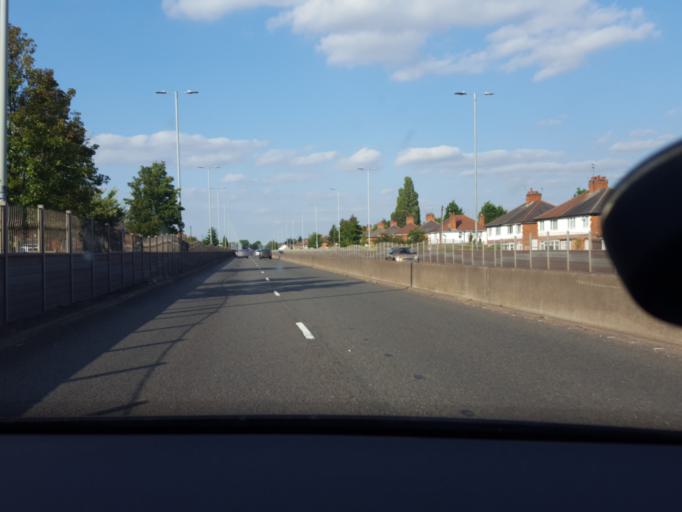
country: GB
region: England
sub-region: Leicestershire
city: Blaby
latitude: 52.6064
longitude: -1.1732
